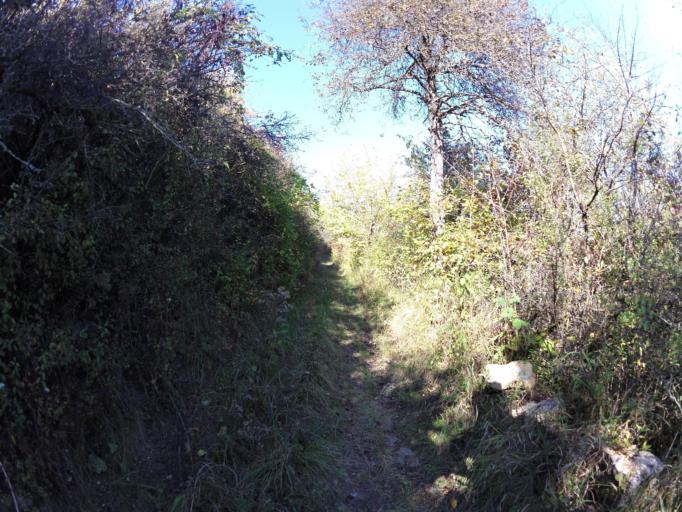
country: DE
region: Bavaria
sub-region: Regierungsbezirk Unterfranken
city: Ochsenfurt
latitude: 49.6798
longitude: 10.0467
